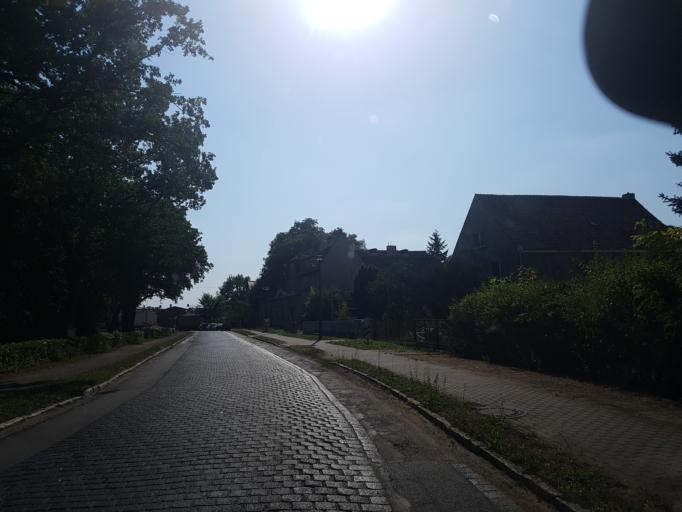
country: DE
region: Saxony-Anhalt
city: Annaburg
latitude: 51.7282
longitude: 13.0374
